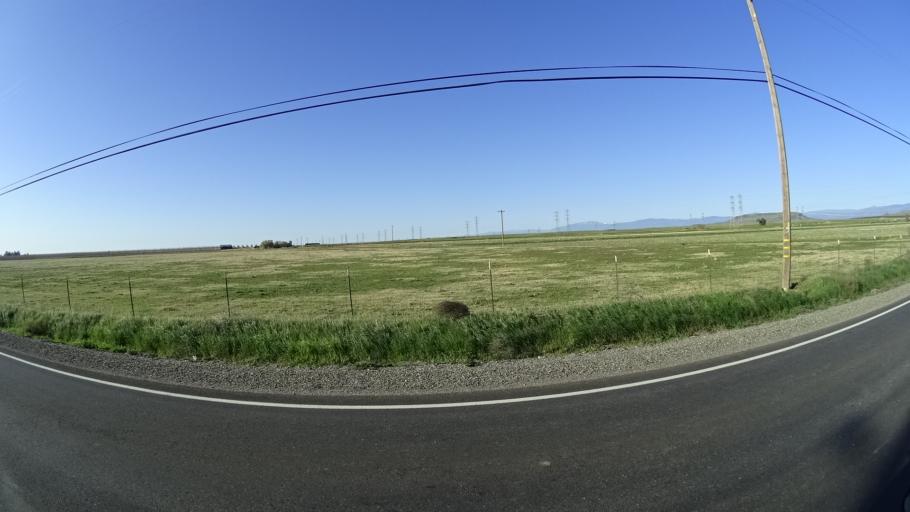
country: US
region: California
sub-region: Glenn County
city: Orland
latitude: 39.7710
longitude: -122.2607
